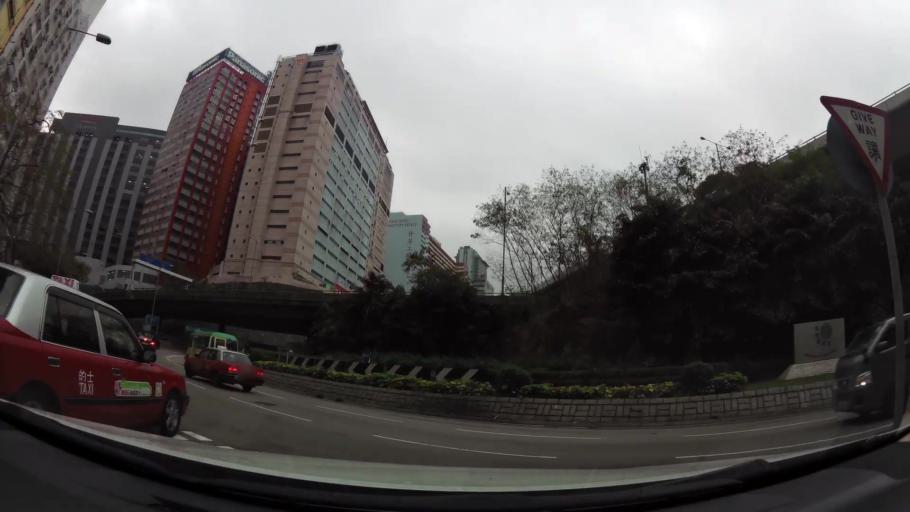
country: HK
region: Tsuen Wan
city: Tsuen Wan
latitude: 22.3636
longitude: 114.1175
